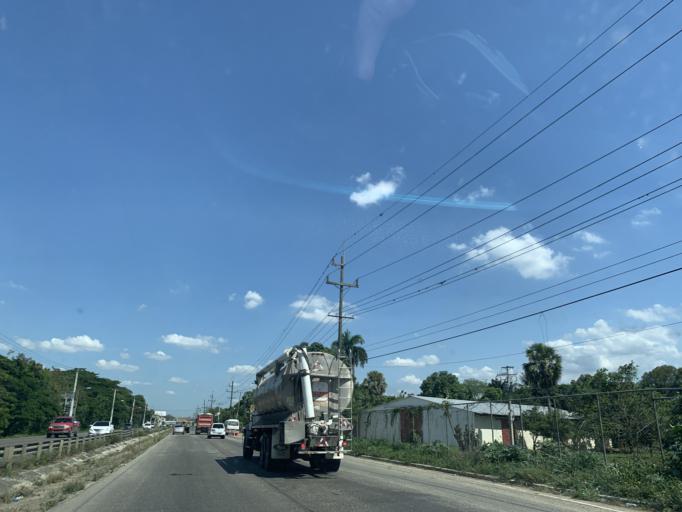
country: DO
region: Santiago
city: Villa Gonzalez
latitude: 19.5229
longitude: -70.7684
